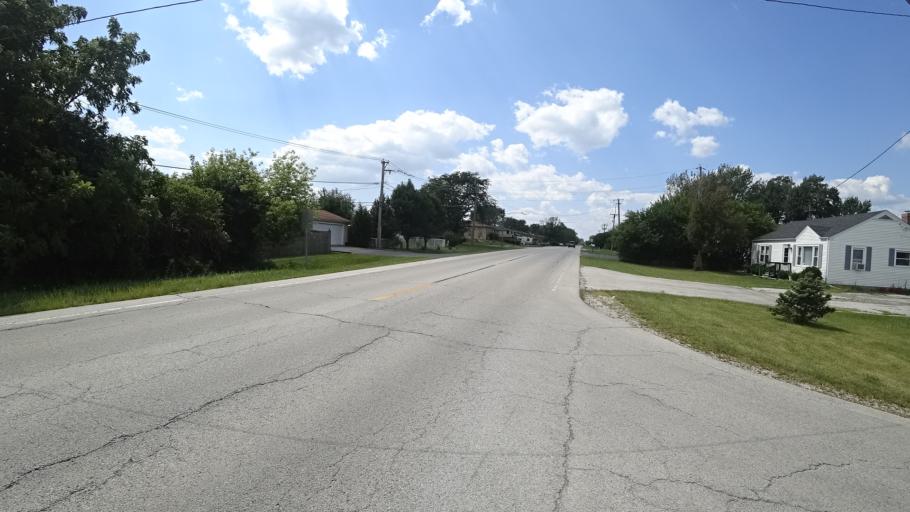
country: US
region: Illinois
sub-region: Cook County
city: Oak Forest
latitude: 41.6173
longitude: -87.7750
